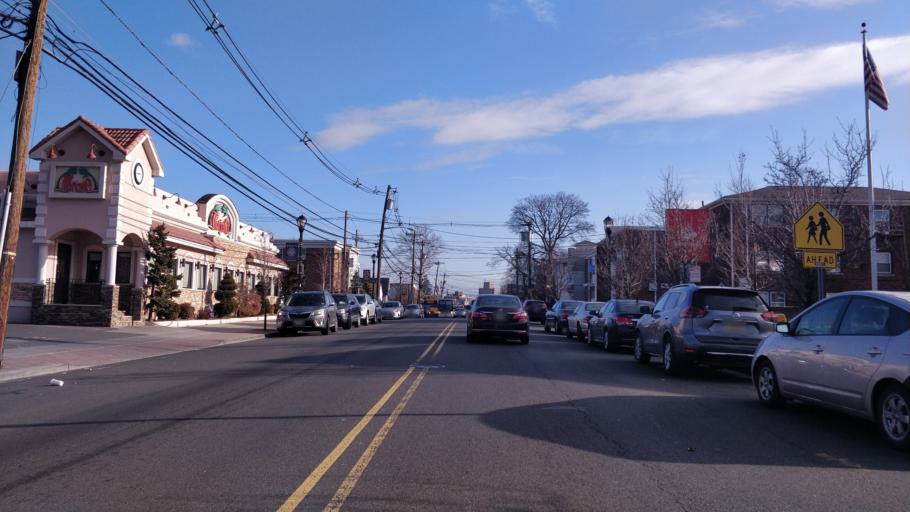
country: US
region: New Jersey
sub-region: Union County
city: Elizabeth
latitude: 40.6737
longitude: -74.2241
